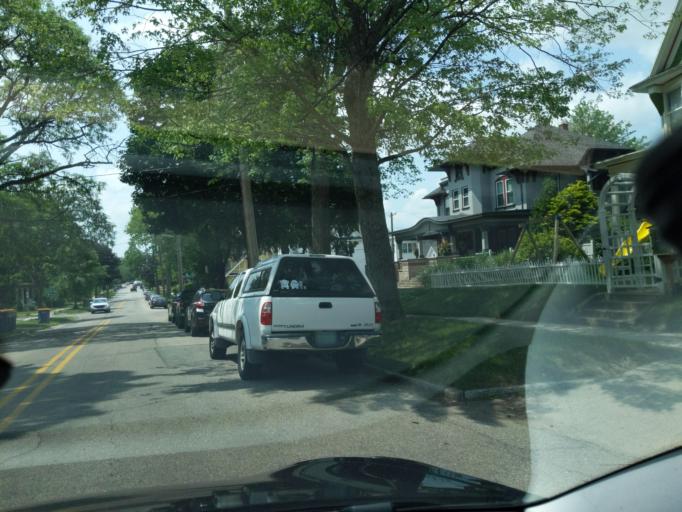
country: US
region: Michigan
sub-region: Kent County
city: East Grand Rapids
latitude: 42.9579
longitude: -85.6313
